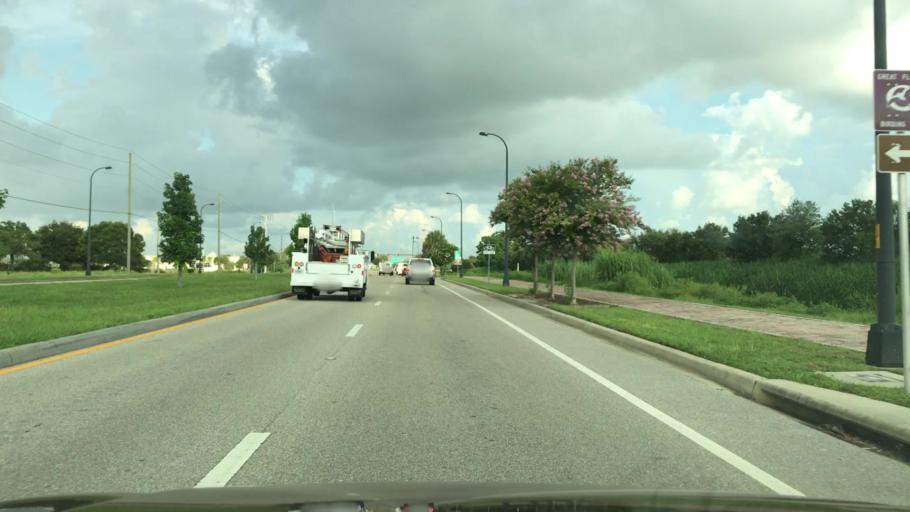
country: US
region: Florida
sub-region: Sarasota County
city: Fruitville
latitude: 27.3386
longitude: -82.4341
